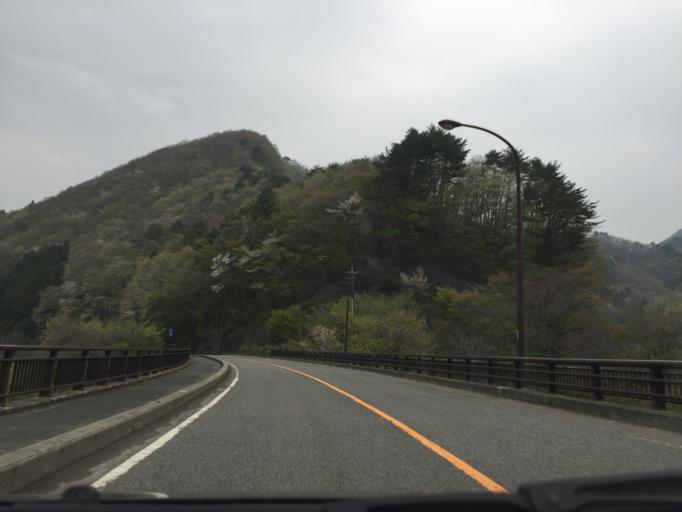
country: JP
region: Tochigi
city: Nikko
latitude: 36.9479
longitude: 139.7005
